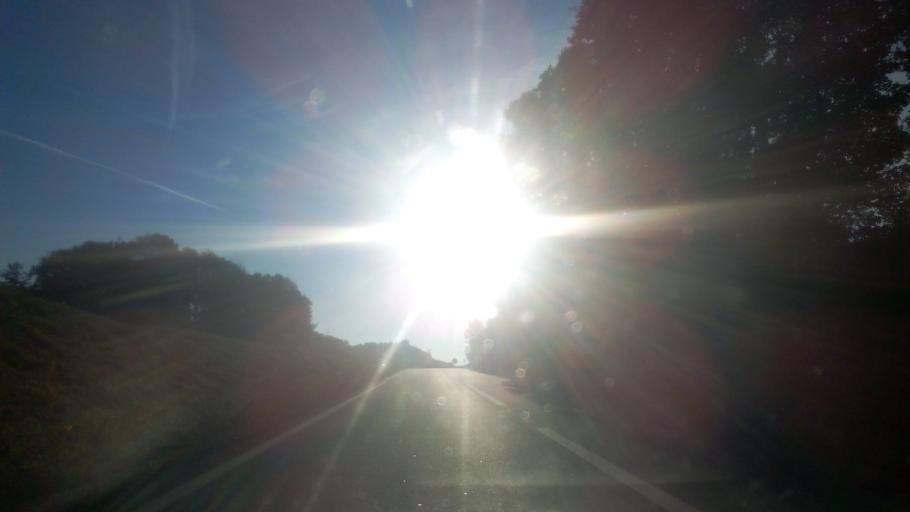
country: FR
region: Brittany
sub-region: Departement du Morbihan
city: Elven
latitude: 47.7231
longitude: -2.5941
